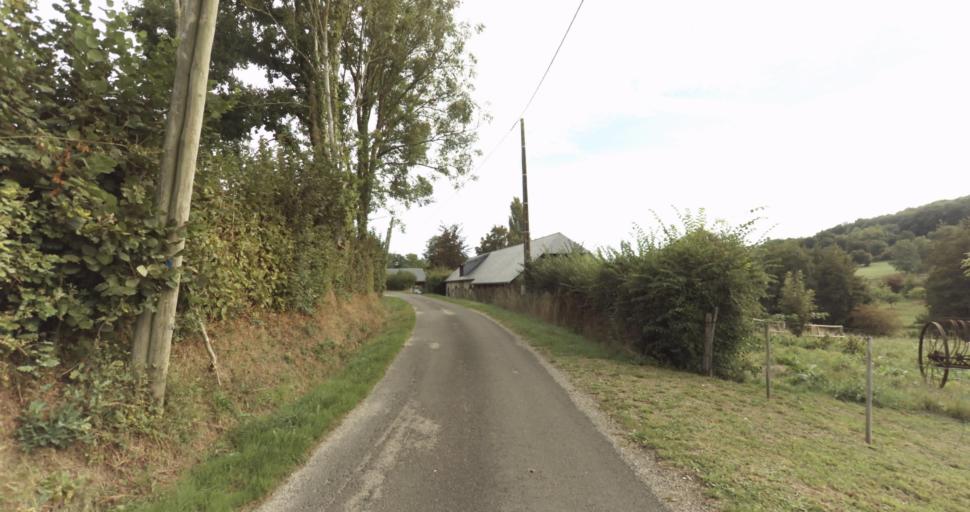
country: FR
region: Lower Normandy
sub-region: Departement de l'Orne
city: Gace
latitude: 48.8344
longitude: 0.2228
